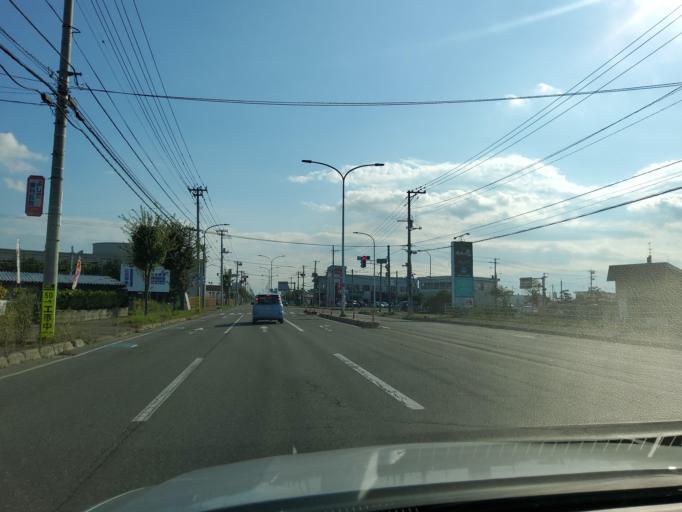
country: JP
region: Hokkaido
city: Obihiro
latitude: 42.8927
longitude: 143.2065
